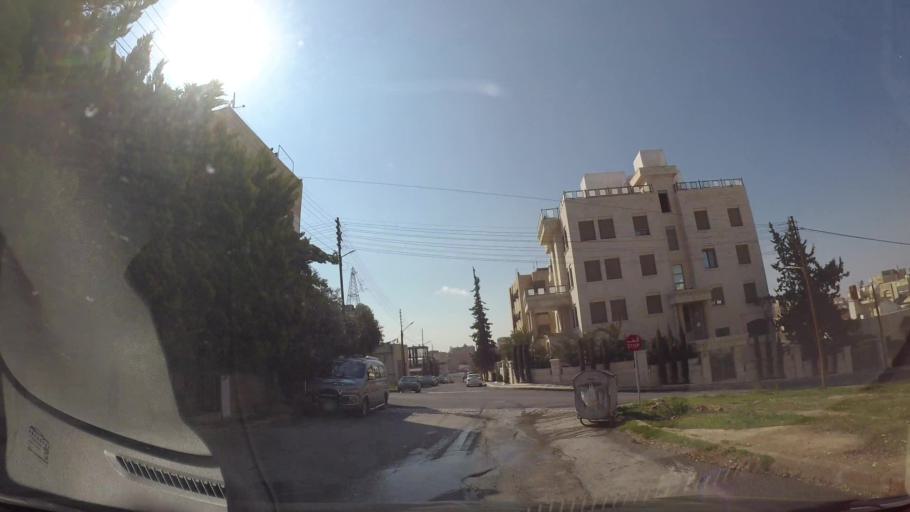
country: JO
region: Amman
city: Al Jubayhah
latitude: 31.9972
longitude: 35.8987
